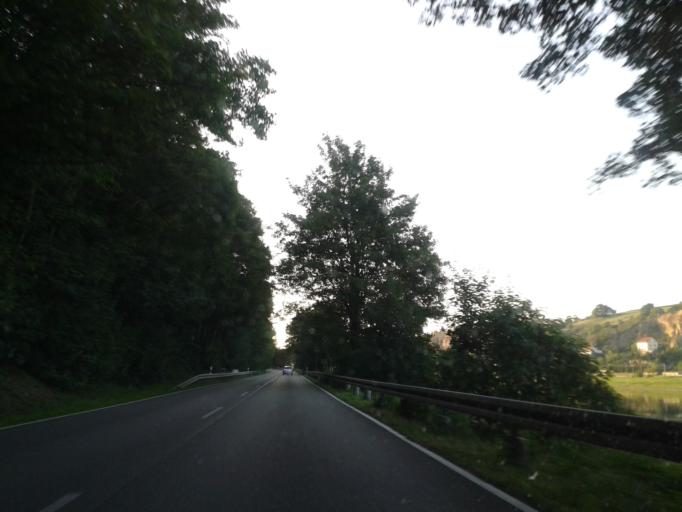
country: DE
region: Saxony
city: Meissen
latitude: 51.1805
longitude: 13.4534
